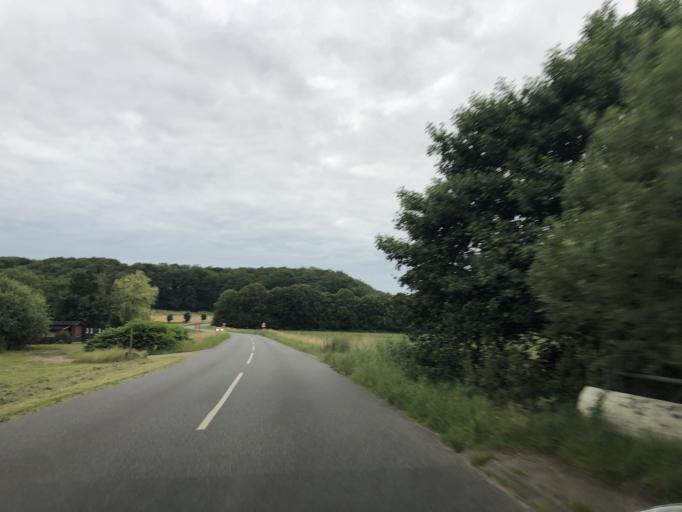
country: DK
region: South Denmark
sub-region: Vejle Kommune
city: Jelling
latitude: 55.7368
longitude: 9.4180
